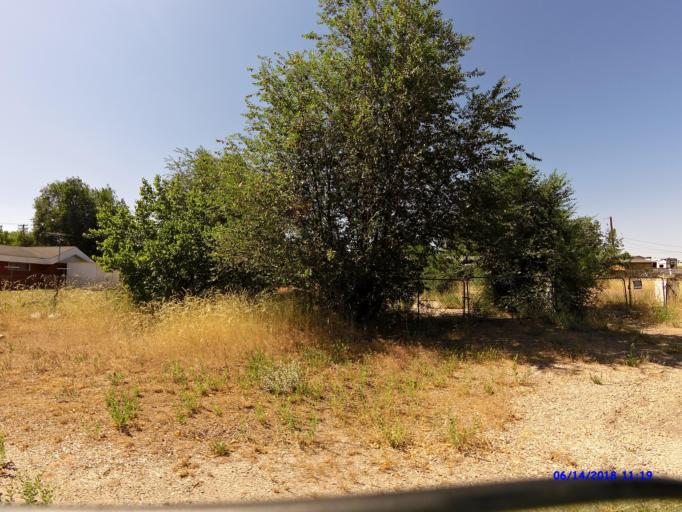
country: US
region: Utah
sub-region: Weber County
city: Ogden
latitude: 41.2186
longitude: -112.0015
